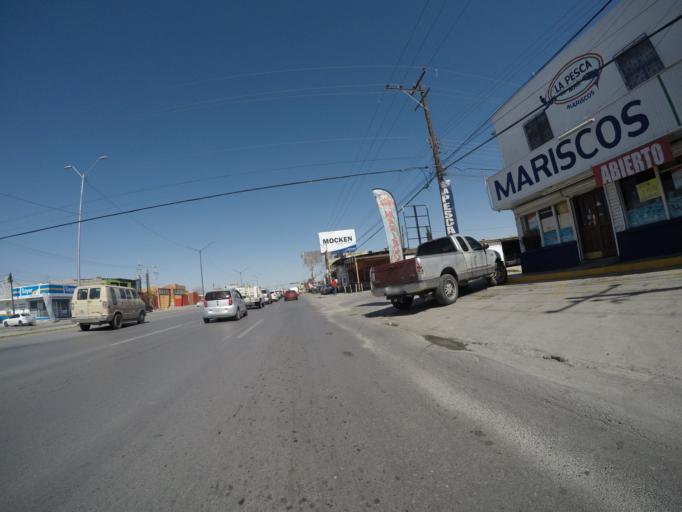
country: MX
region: Chihuahua
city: Ciudad Juarez
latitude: 31.7051
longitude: -106.4465
